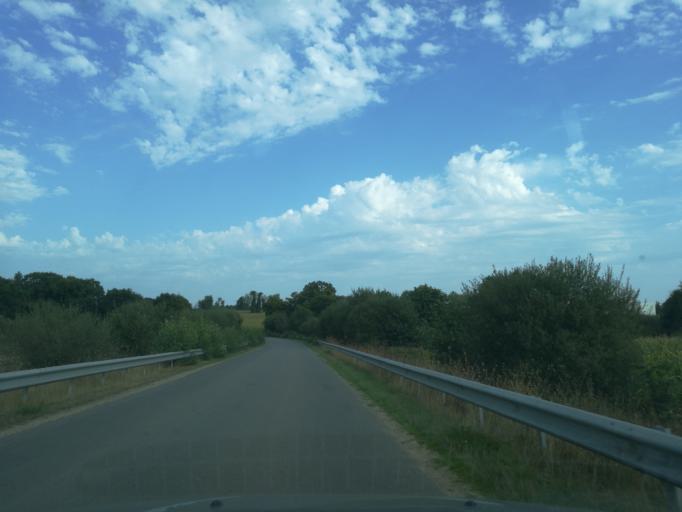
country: FR
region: Brittany
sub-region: Departement d'Ille-et-Vilaine
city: Bedee
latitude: 48.1870
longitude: -1.9503
